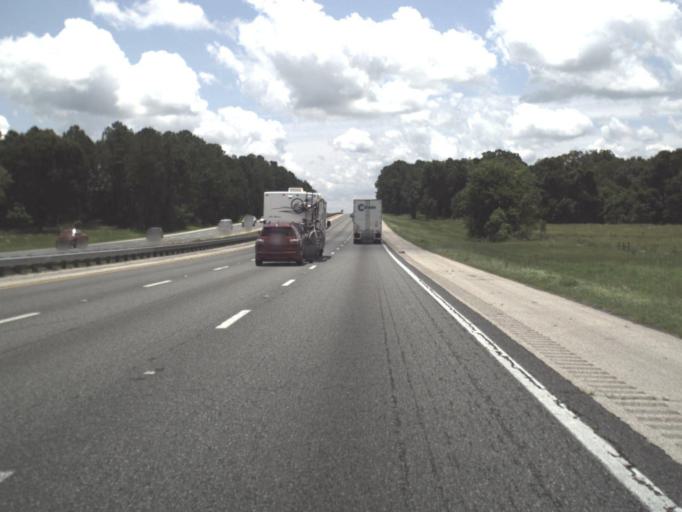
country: US
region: Florida
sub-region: Alachua County
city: High Springs
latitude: 29.8532
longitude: -82.5363
